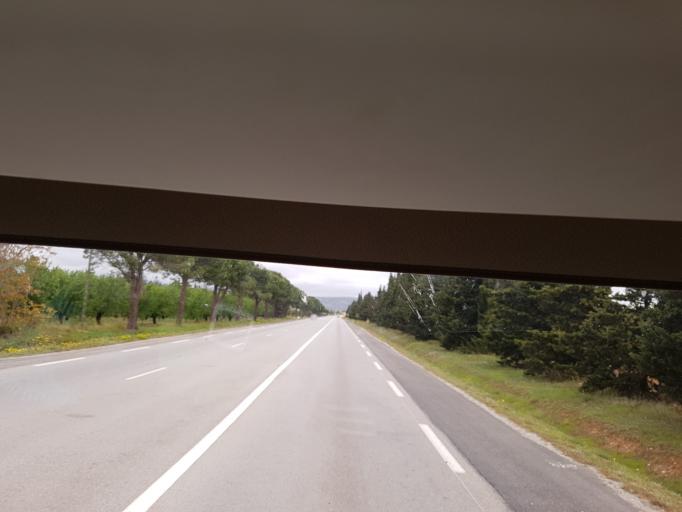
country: FR
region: Languedoc-Roussillon
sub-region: Departement des Pyrenees-Orientales
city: Salses-le-Chateau
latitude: 42.8164
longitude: 2.9149
